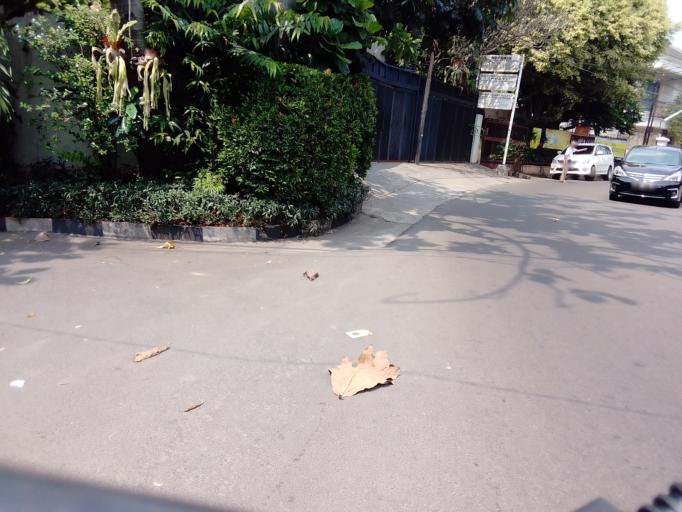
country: ID
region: Jakarta Raya
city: Jakarta
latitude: -6.2117
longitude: 106.8109
